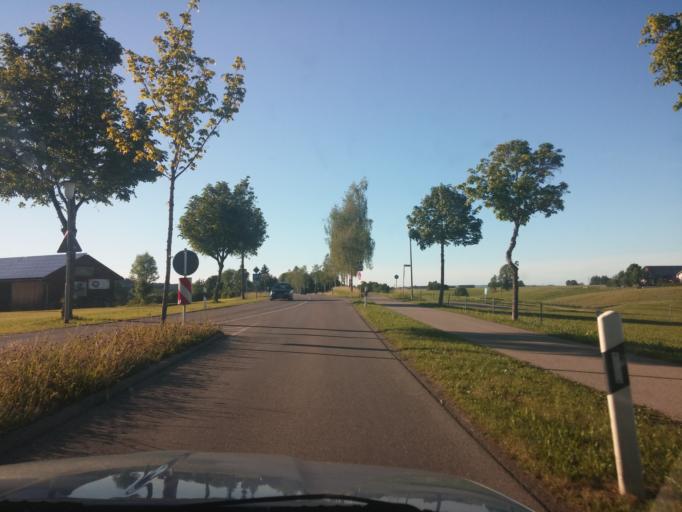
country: DE
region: Bavaria
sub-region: Swabia
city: Woringen
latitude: 47.8821
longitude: 10.2149
